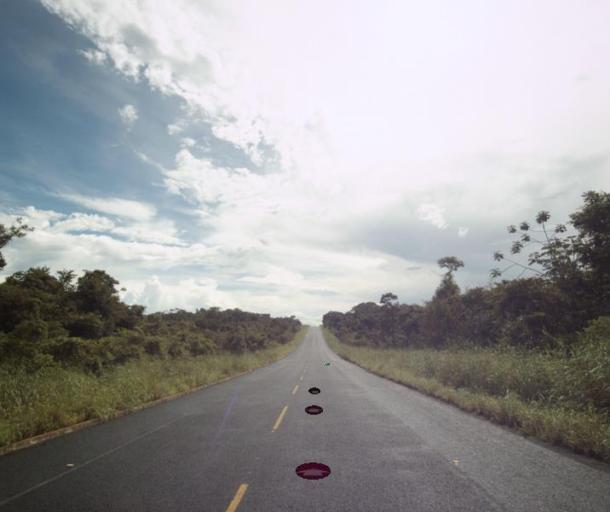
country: BR
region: Goias
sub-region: Sao Miguel Do Araguaia
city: Sao Miguel do Araguaia
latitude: -13.2983
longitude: -50.3270
